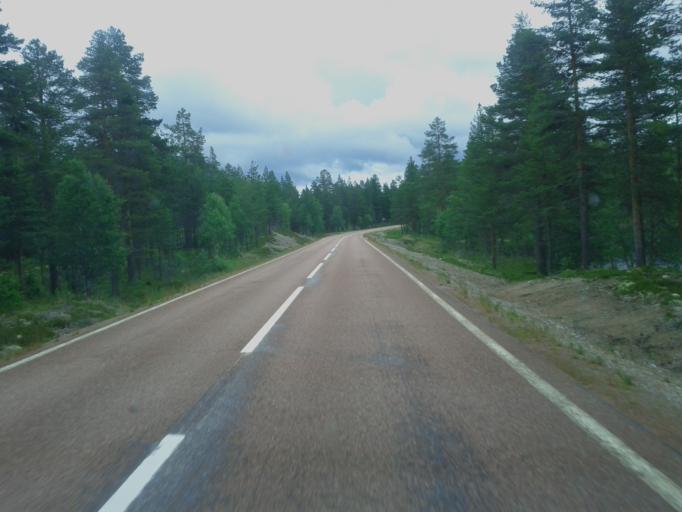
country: NO
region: Hedmark
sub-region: Engerdal
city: Engerdal
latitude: 61.8079
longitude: 12.4143
